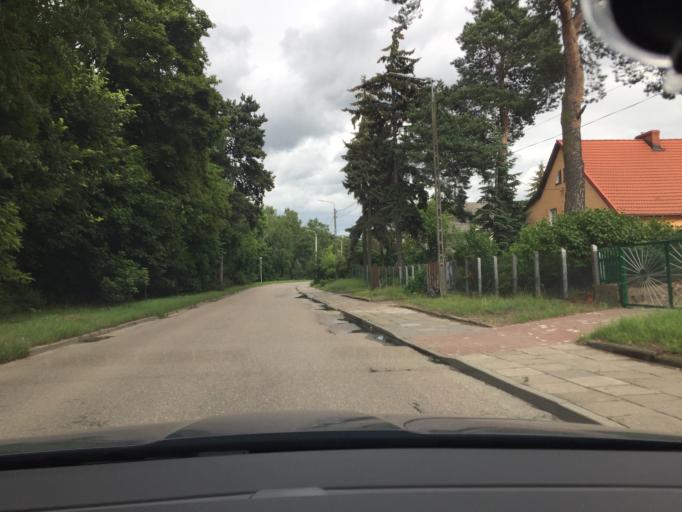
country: PL
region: Pomeranian Voivodeship
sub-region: Gdansk
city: Gdansk
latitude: 54.3619
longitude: 18.7236
